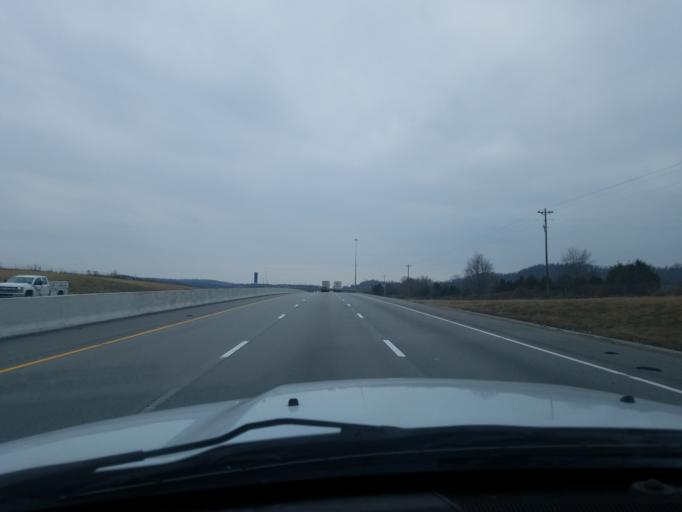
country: US
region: Kentucky
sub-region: Hart County
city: Munfordville
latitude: 37.2484
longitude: -85.9260
